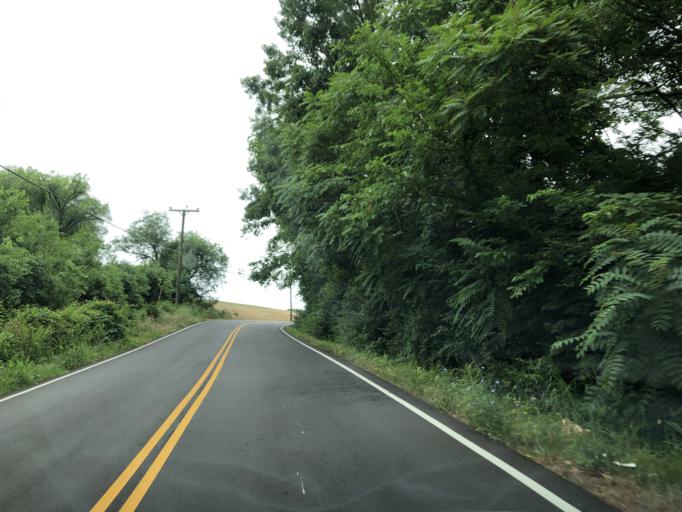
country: US
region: Tennessee
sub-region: Davidson County
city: Goodlettsville
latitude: 36.2949
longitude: -86.7544
